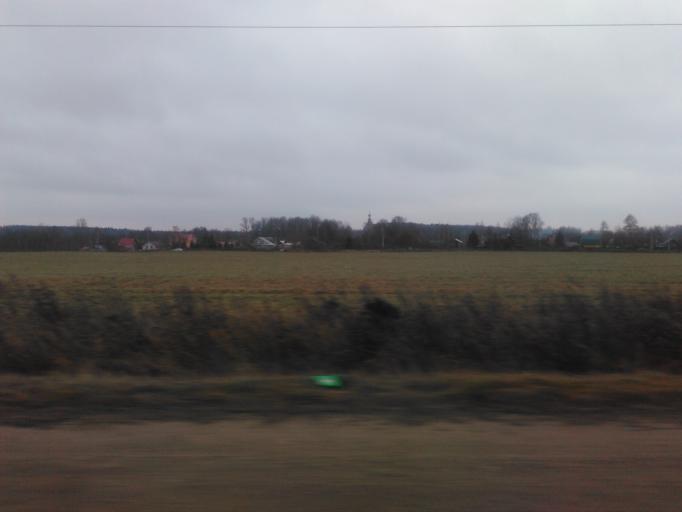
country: RU
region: Moskovskaya
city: Ashukino
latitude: 56.1552
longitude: 37.9743
